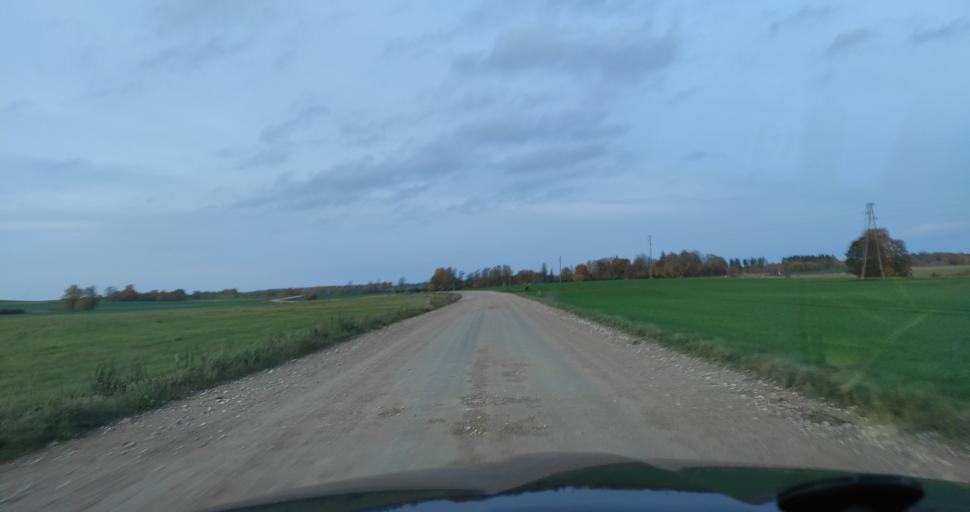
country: LV
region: Aizpute
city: Aizpute
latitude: 56.6785
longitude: 21.7927
